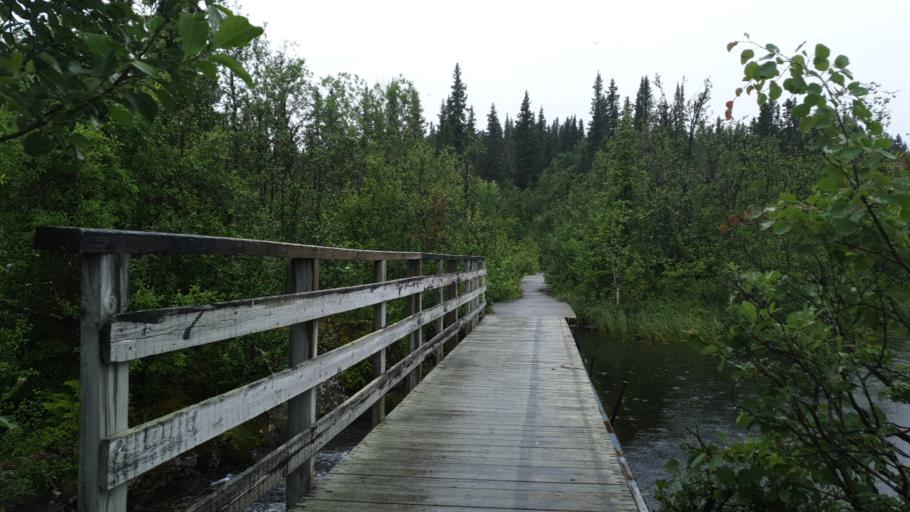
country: NO
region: Oppland
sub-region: Vestre Slidre
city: Slidre
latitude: 61.2297
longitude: 8.9235
